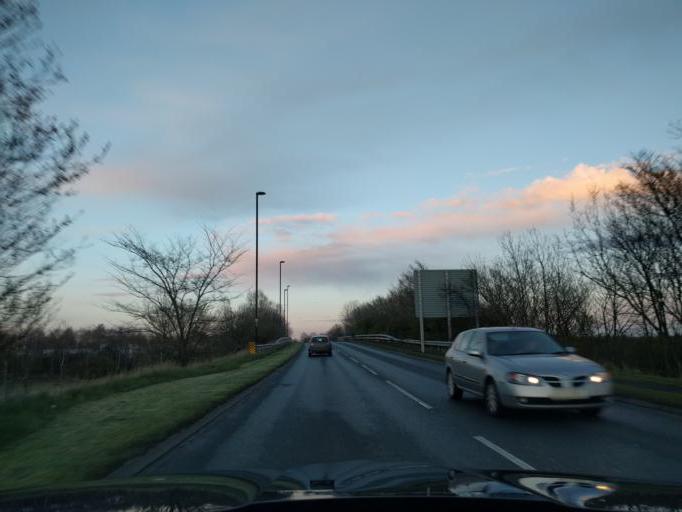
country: GB
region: England
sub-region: Northumberland
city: Seghill
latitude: 55.0393
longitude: -1.5892
